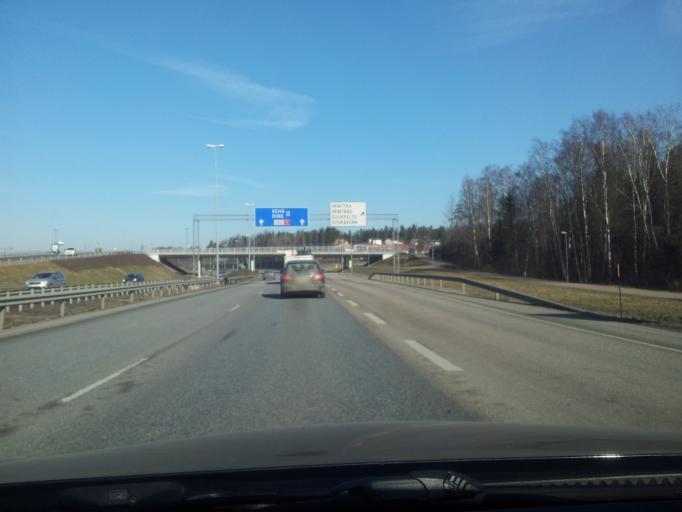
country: FI
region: Uusimaa
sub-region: Helsinki
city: Kauniainen
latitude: 60.1858
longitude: 24.7492
